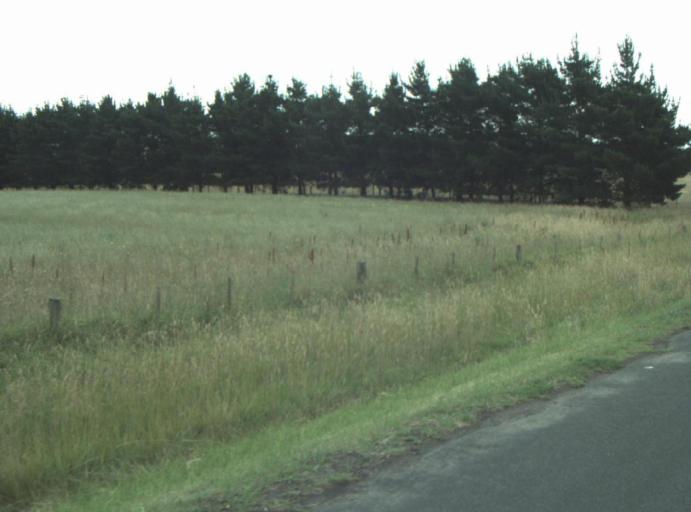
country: AU
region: Victoria
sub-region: Greater Geelong
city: Clifton Springs
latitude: -38.1816
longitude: 144.5185
